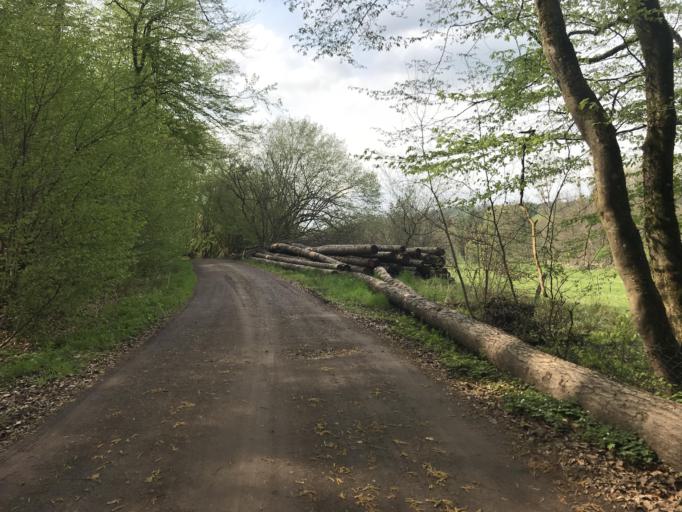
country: DE
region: Hesse
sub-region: Regierungsbezirk Giessen
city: Laubach
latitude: 50.5126
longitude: 9.0060
